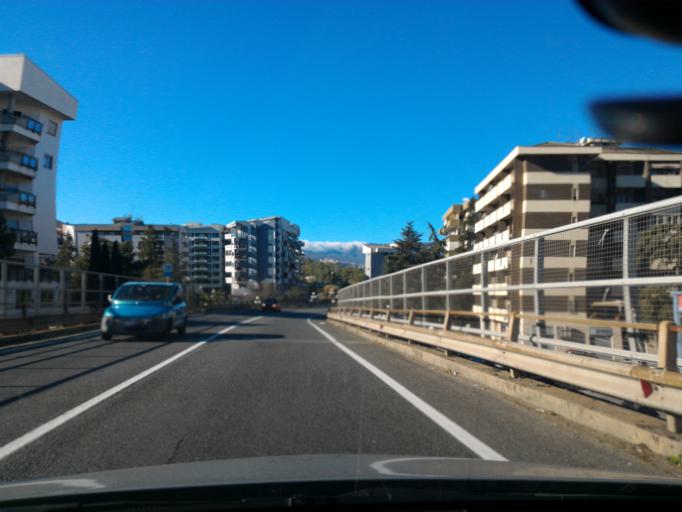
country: IT
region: Calabria
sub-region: Provincia di Cosenza
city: Quattromiglia
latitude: 39.3321
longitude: 16.2418
